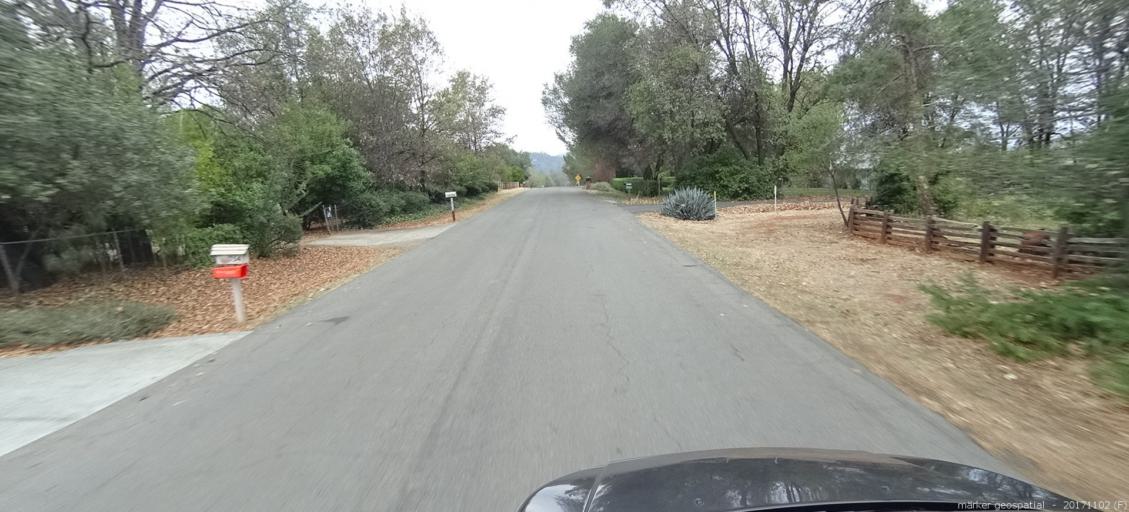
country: US
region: California
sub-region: Shasta County
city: Shasta Lake
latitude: 40.6595
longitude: -122.3104
